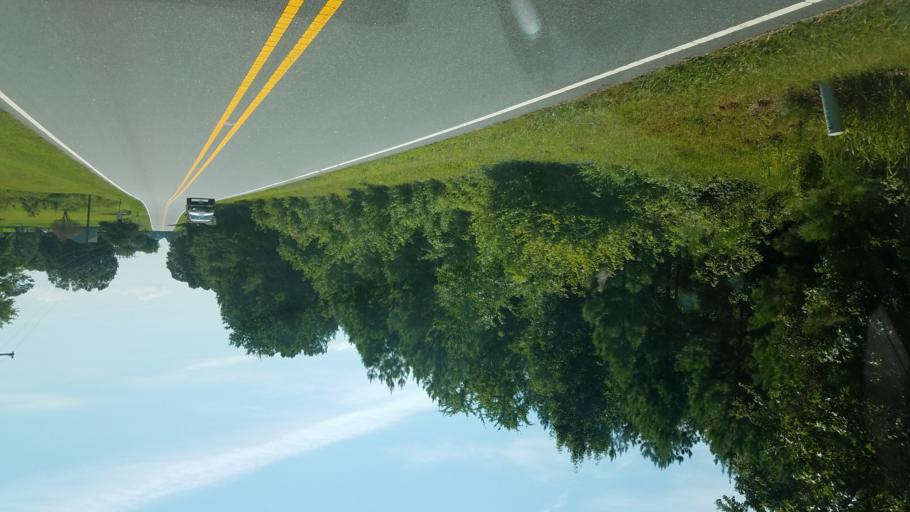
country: US
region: North Carolina
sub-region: Gaston County
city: Cherryville
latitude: 35.5133
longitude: -81.4669
